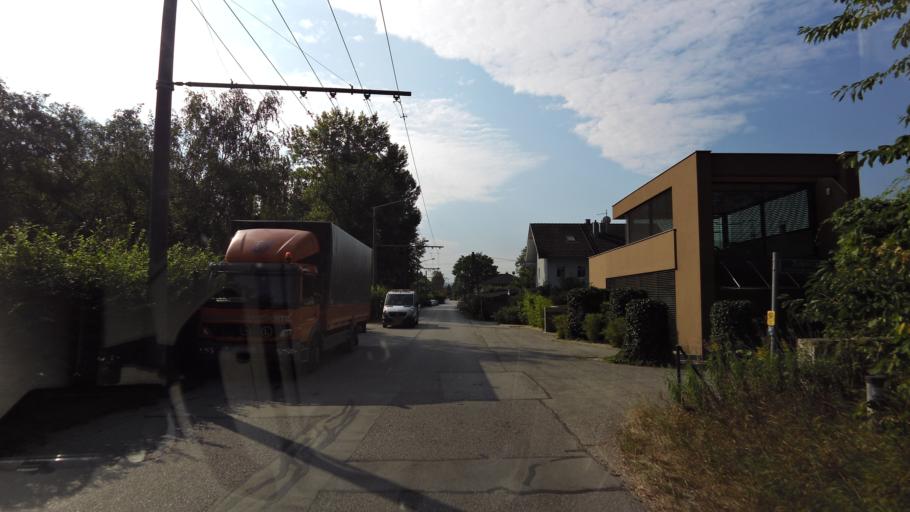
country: AT
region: Salzburg
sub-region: Politischer Bezirk Salzburg-Umgebung
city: Bergheim
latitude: 47.8339
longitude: 13.0177
